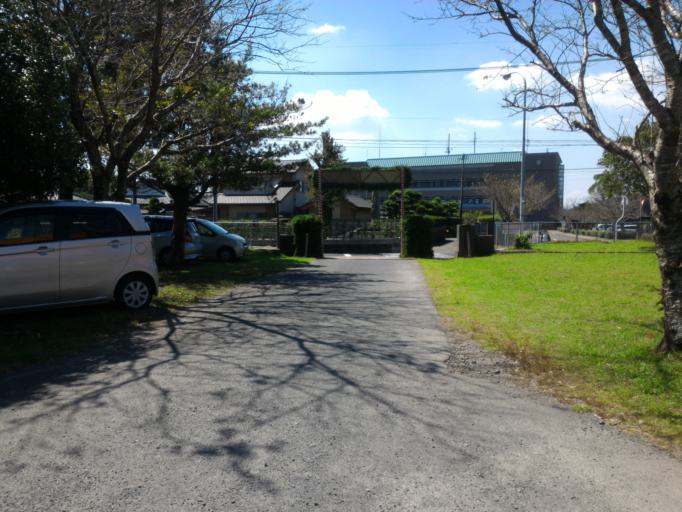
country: JP
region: Kagoshima
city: Kanoya
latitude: 31.3859
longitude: 130.9749
